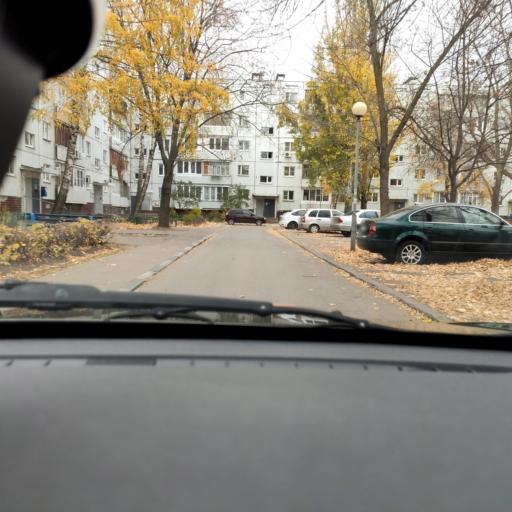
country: RU
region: Samara
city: Tol'yatti
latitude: 53.5345
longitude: 49.2949
